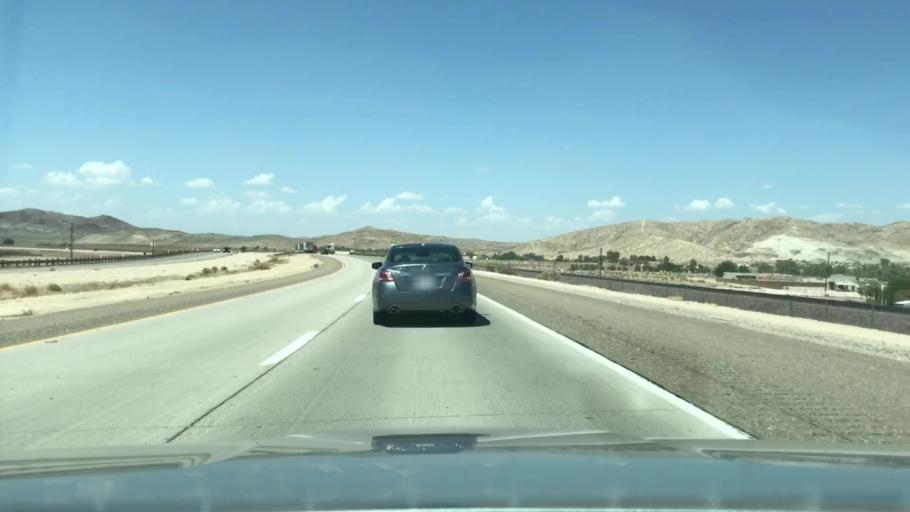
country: US
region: California
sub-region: San Bernardino County
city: Lenwood
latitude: 34.9043
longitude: -117.0936
